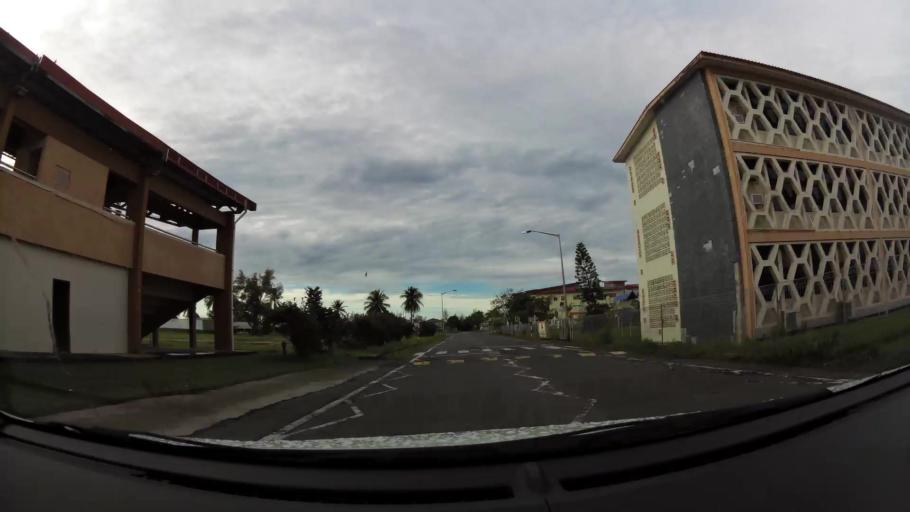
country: BN
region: Belait
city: Seria
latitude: 4.6094
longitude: 114.3319
